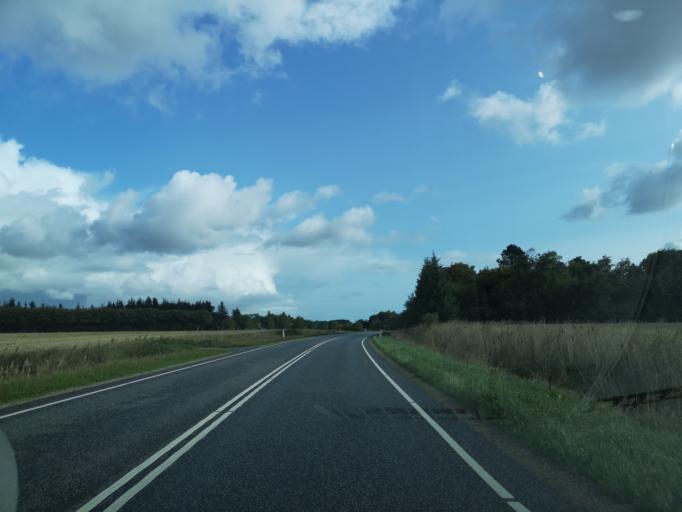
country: DK
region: Central Jutland
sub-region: Ringkobing-Skjern Kommune
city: Videbaek
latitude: 56.0379
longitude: 8.6111
